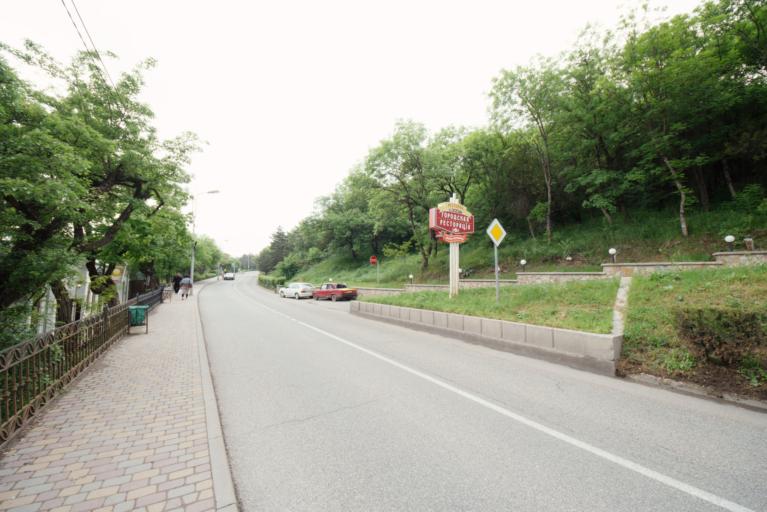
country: RU
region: Stavropol'skiy
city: Goryachevodskiy
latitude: 44.0408
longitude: 43.0891
